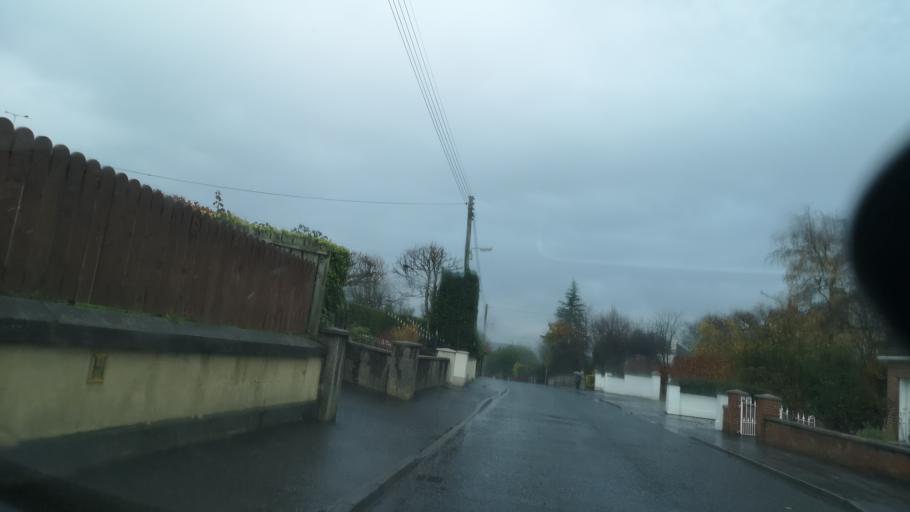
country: GB
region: Northern Ireland
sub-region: Newry and Mourne District
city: Newry
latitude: 54.1795
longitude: -6.3263
